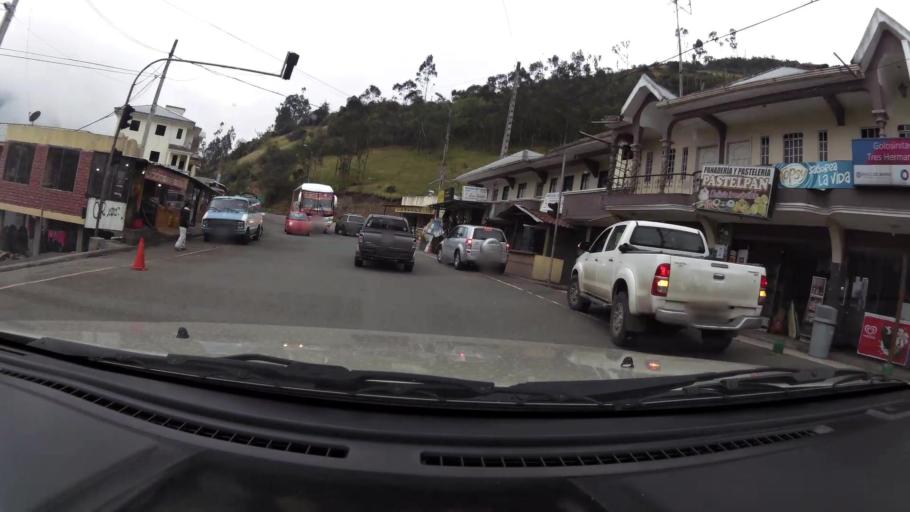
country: EC
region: Canar
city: Canar
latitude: -2.4597
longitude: -79.0040
